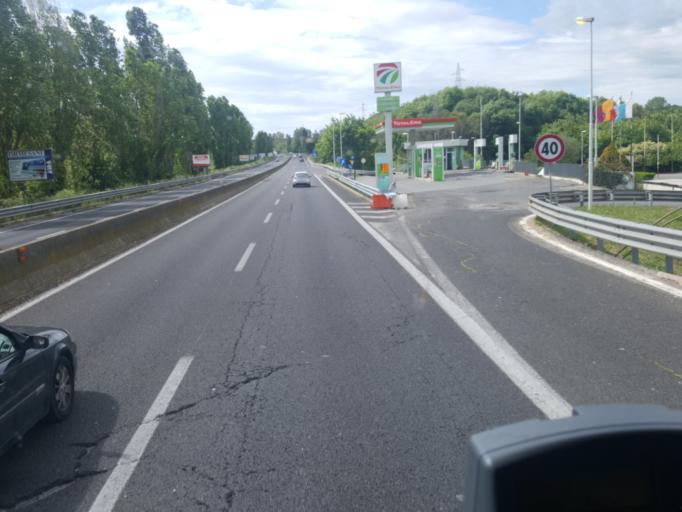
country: IT
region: Latium
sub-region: Citta metropolitana di Roma Capitale
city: Valle Santa
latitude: 41.8918
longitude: 12.2964
